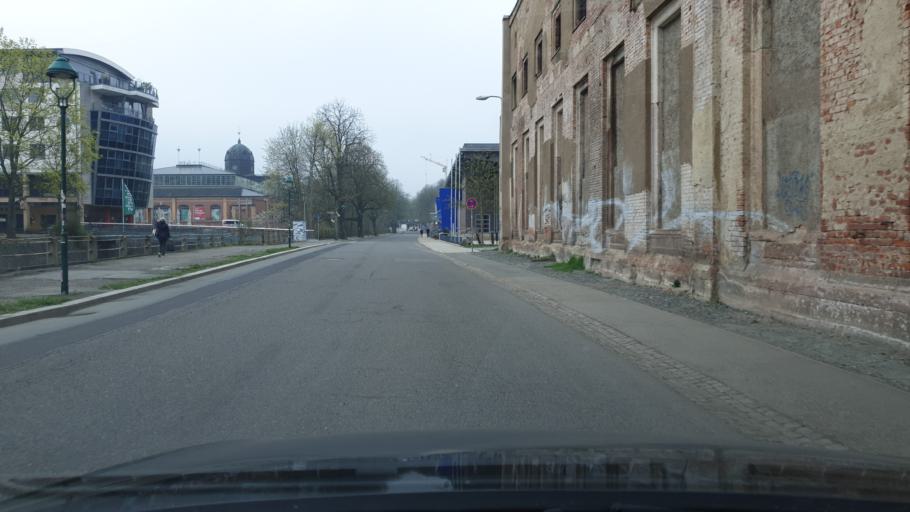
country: DE
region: Saxony
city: Chemnitz
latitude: 50.8372
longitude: 12.9149
